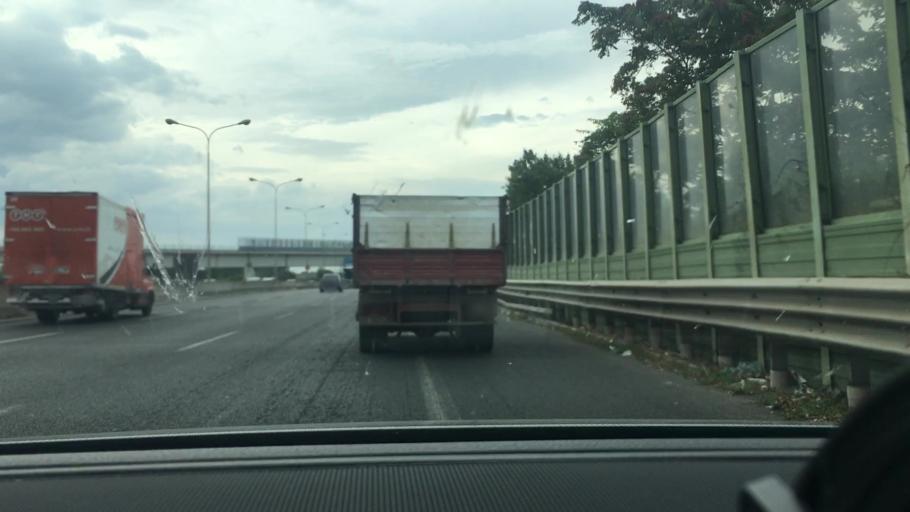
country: IT
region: Apulia
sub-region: Provincia di Bari
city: Bari
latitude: 41.0922
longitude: 16.8463
